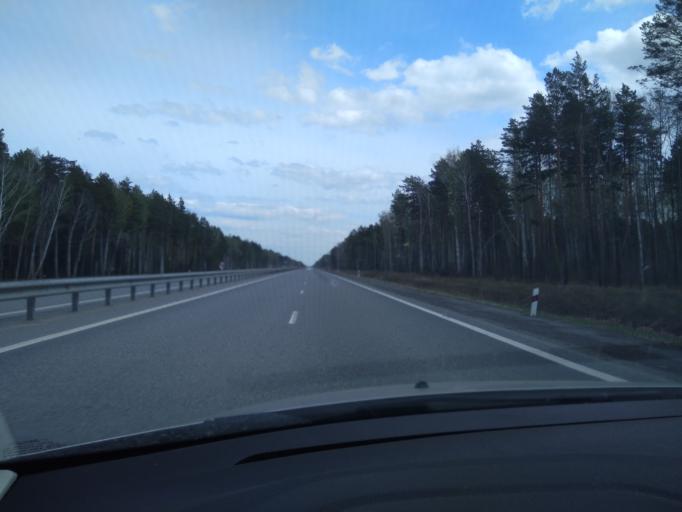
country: RU
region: Sverdlovsk
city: Yushala
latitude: 57.0903
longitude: 64.4187
